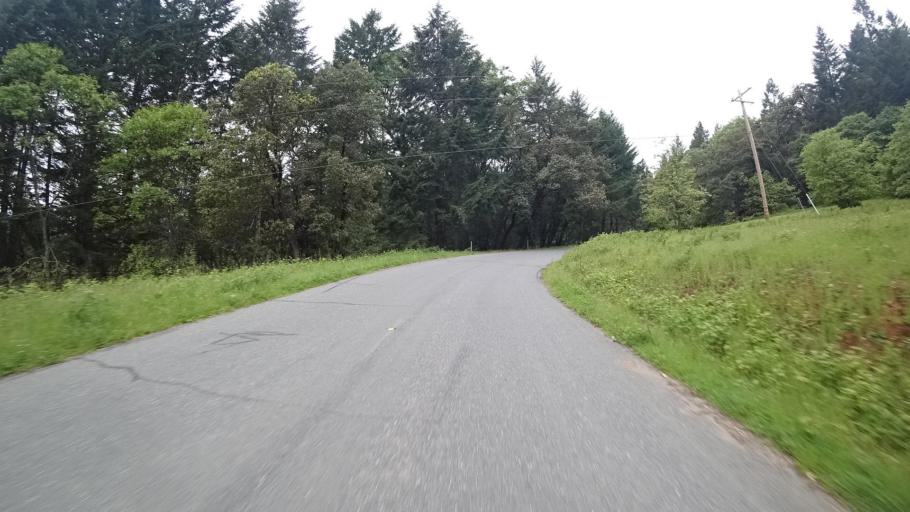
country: US
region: California
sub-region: Humboldt County
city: Willow Creek
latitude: 41.1107
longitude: -123.7117
